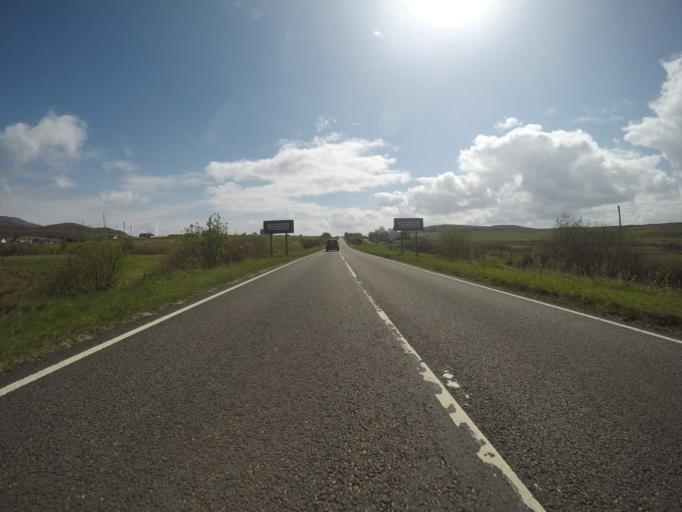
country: GB
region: Scotland
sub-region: Highland
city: Portree
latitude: 57.4789
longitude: -6.3002
